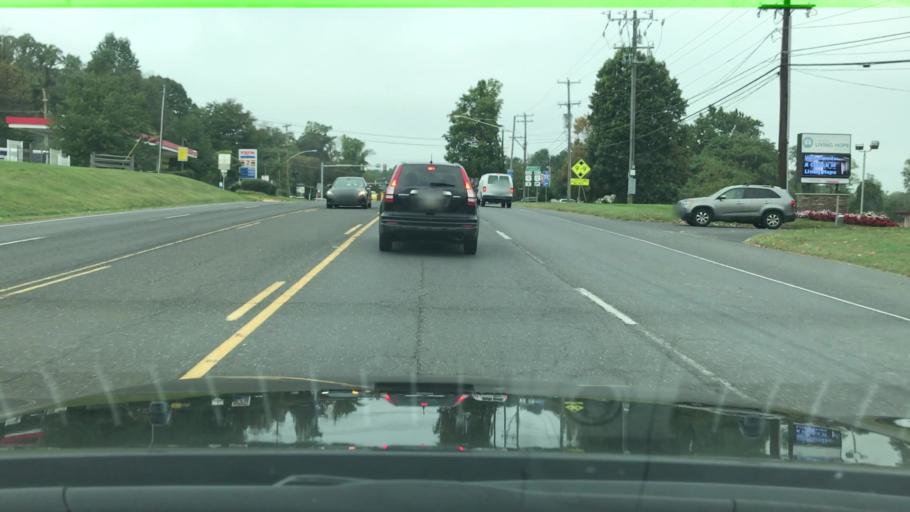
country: US
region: Pennsylvania
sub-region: Bucks County
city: Langhorne Manor
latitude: 40.1776
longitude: -74.9022
